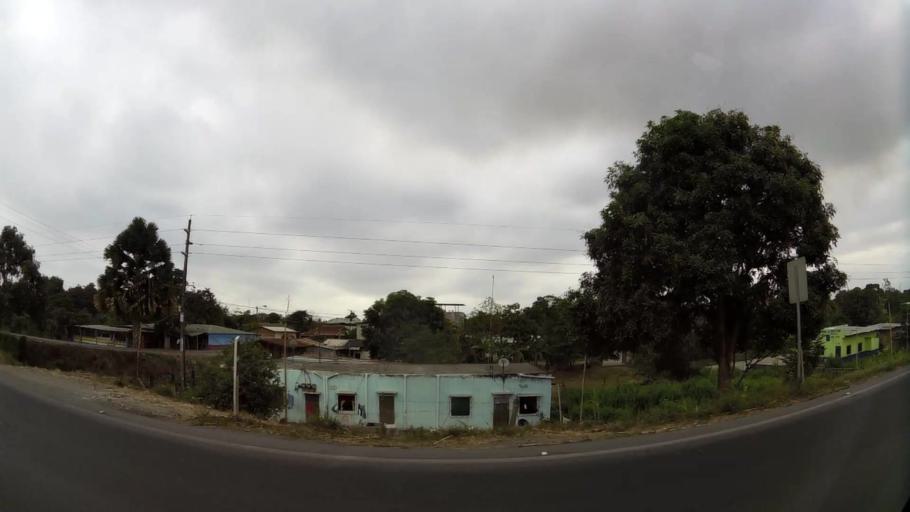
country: EC
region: Guayas
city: Yaguachi Nuevo
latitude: -2.2563
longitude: -79.6363
